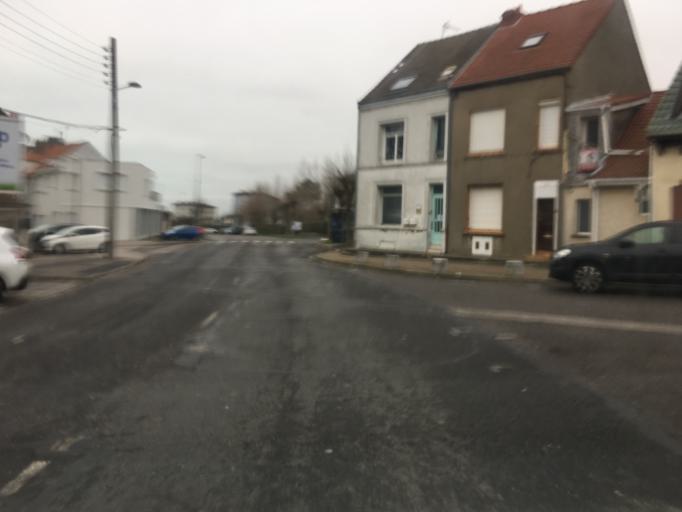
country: FR
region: Nord-Pas-de-Calais
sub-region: Departement du Pas-de-Calais
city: Outreau
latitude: 50.7115
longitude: 1.5920
